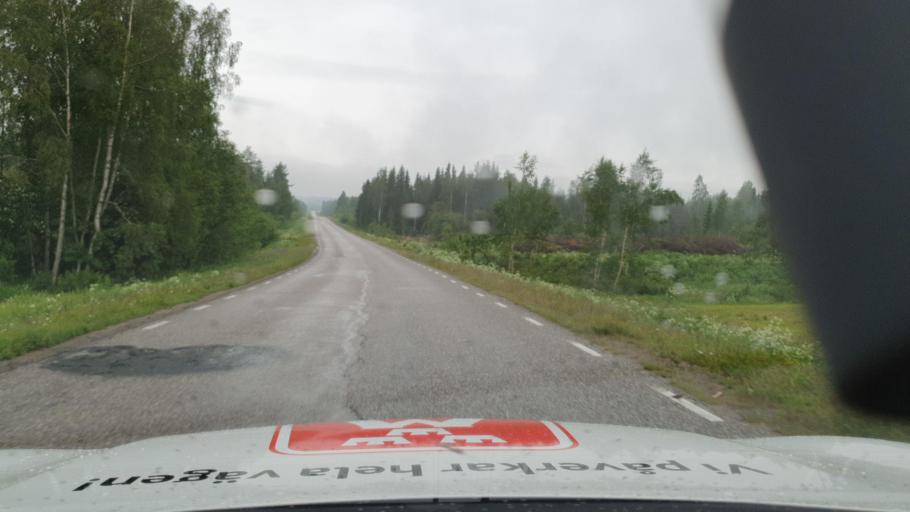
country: SE
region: Vaesterbotten
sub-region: Vannas Kommun
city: Vaennaes
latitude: 63.7787
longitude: 19.5984
